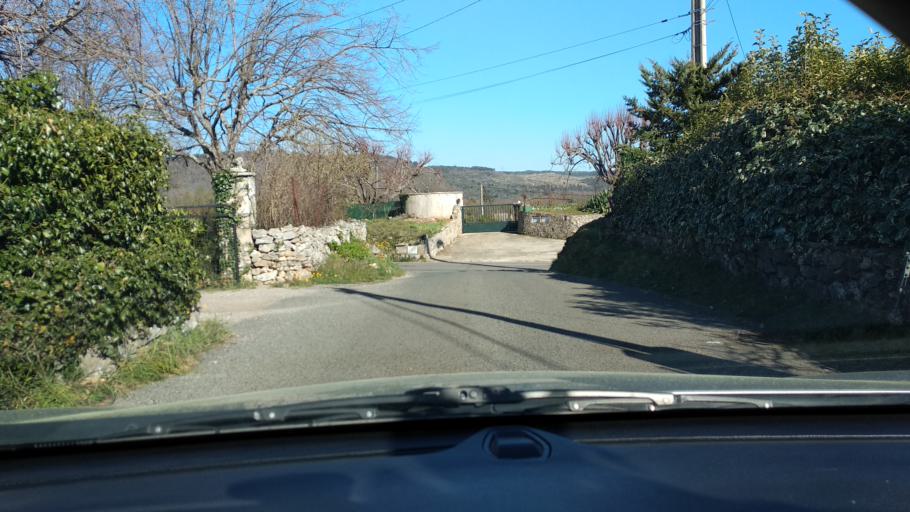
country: FR
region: Provence-Alpes-Cote d'Azur
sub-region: Departement des Alpes-Maritimes
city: Saint-Cezaire-sur-Siagne
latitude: 43.6557
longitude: 6.7918
